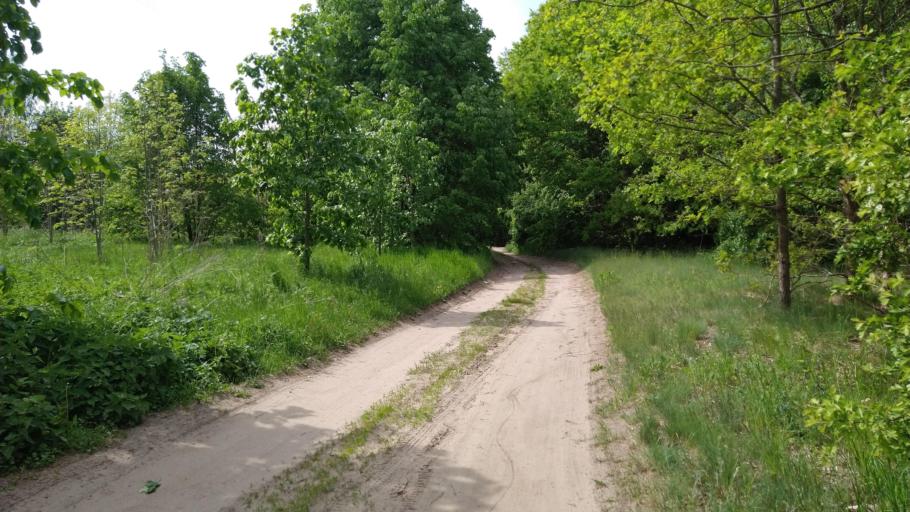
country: PL
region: Warmian-Masurian Voivodeship
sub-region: Powiat olsztynski
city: Olsztyn
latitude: 53.7935
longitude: 20.5438
